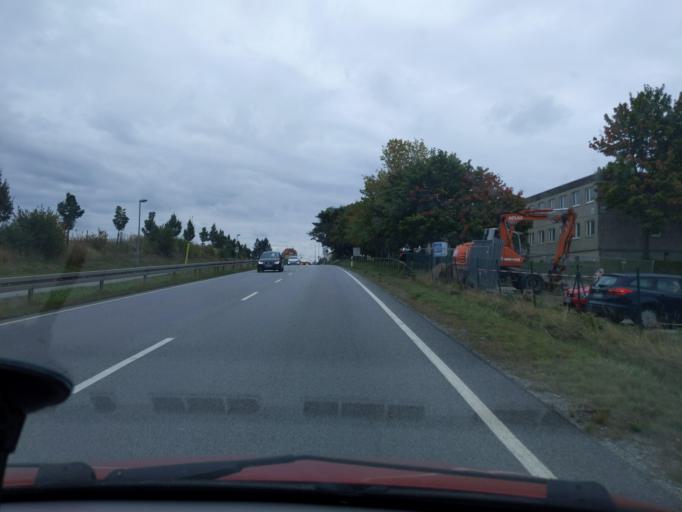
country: DE
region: Saxony
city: Bautzen
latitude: 51.1703
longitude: 14.4148
